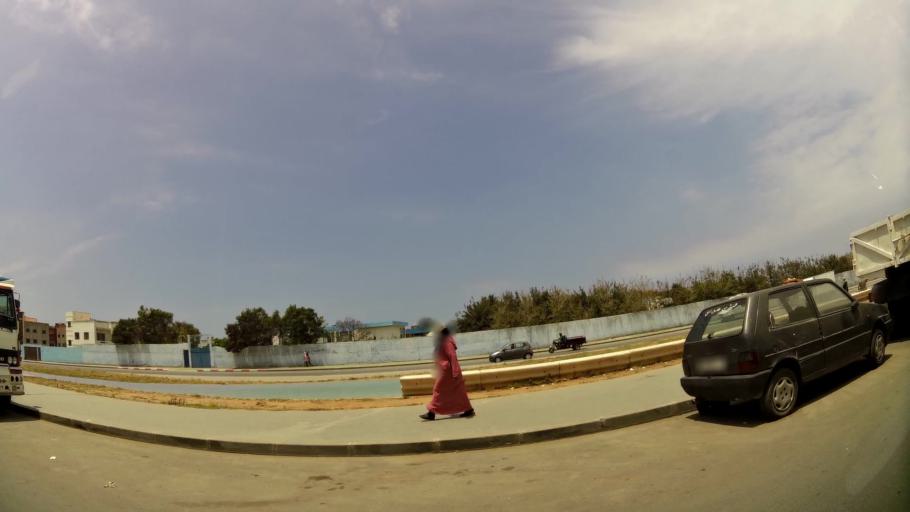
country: MA
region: Rabat-Sale-Zemmour-Zaer
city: Sale
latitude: 34.0663
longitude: -6.7790
